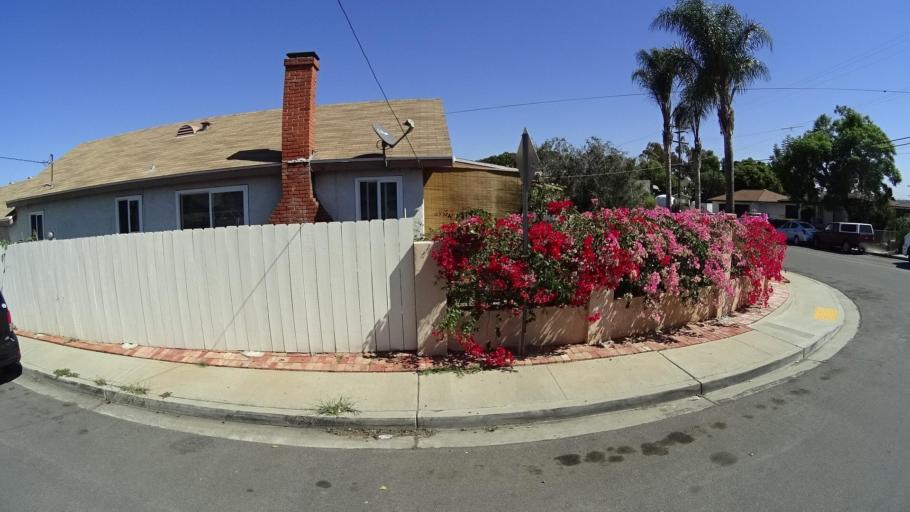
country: US
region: California
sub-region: San Diego County
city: National City
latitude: 32.6654
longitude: -117.0820
